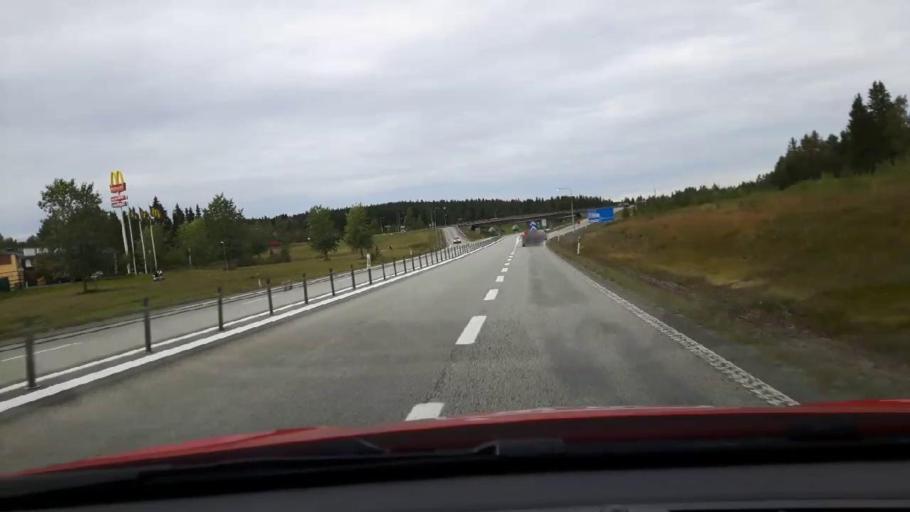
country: SE
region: Jaemtland
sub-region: OEstersunds Kommun
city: Ostersund
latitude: 63.1767
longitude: 14.6952
